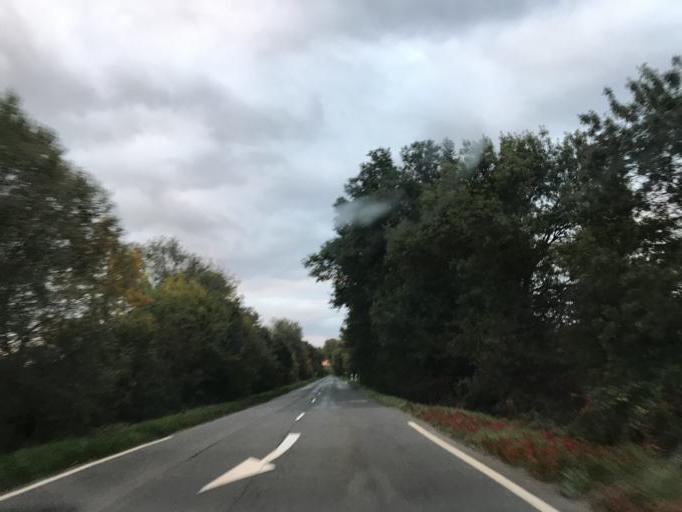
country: FR
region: Rhone-Alpes
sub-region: Departement de l'Ain
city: Trevoux
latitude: 45.9278
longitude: 4.7619
